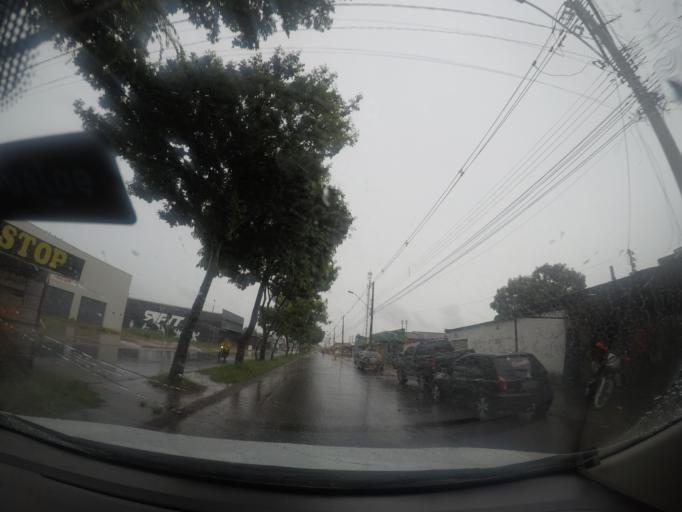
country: BR
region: Goias
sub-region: Goiania
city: Goiania
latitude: -16.6220
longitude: -49.3374
